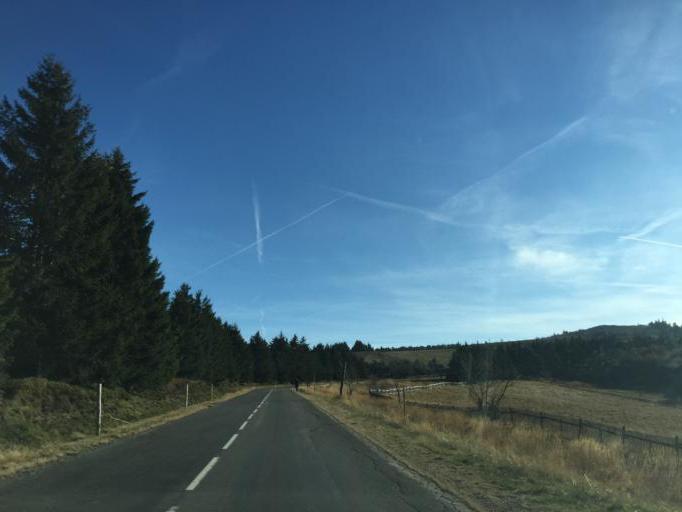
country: FR
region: Rhone-Alpes
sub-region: Departement de la Loire
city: Saint-Julien-Molin-Molette
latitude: 45.3891
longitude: 4.5760
